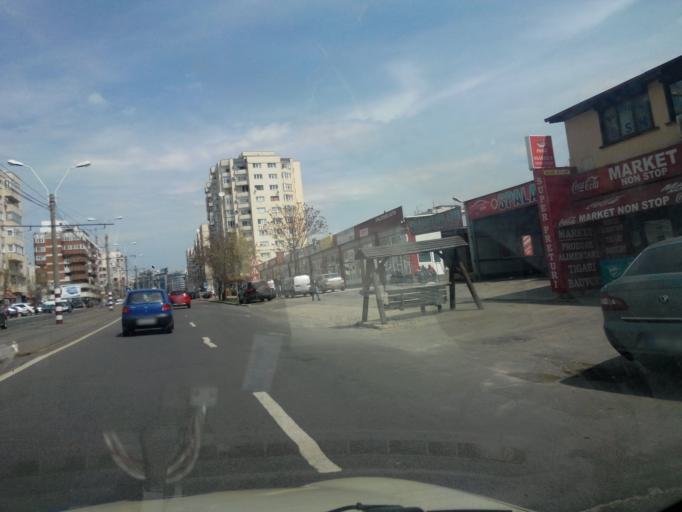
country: RO
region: Bucuresti
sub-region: Municipiul Bucuresti
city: Bucharest
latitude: 44.4185
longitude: 26.1146
